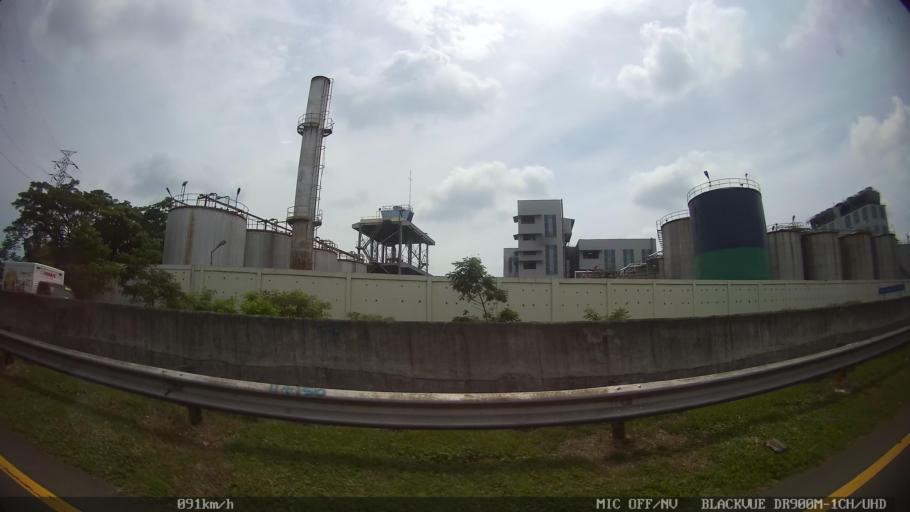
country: ID
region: North Sumatra
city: Labuhan Deli
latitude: 3.6692
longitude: 98.6813
